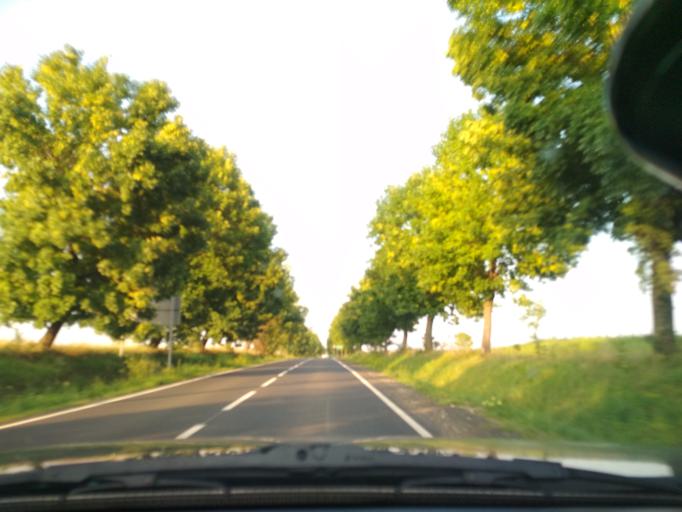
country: PL
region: Silesian Voivodeship
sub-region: Powiat zawiercianski
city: Pilica
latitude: 50.4643
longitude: 19.6004
